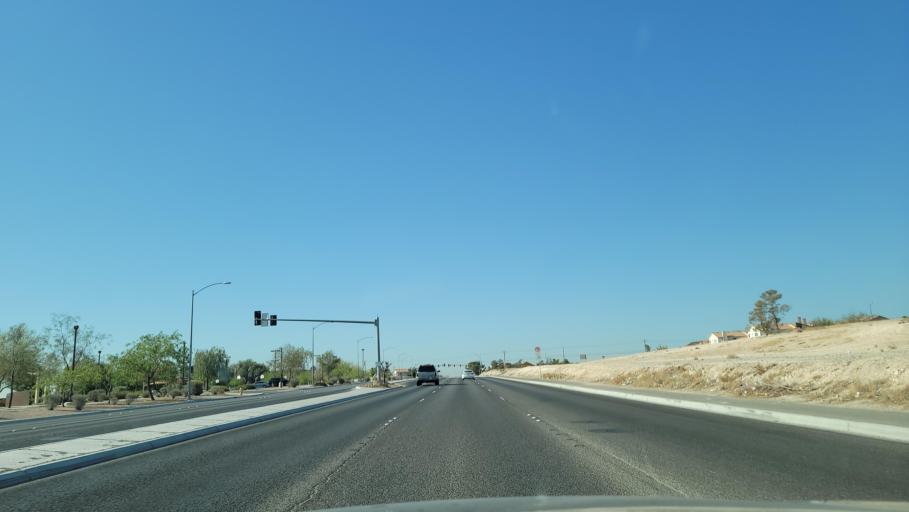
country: US
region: Nevada
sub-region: Clark County
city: Las Vegas
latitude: 36.2282
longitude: -115.1801
